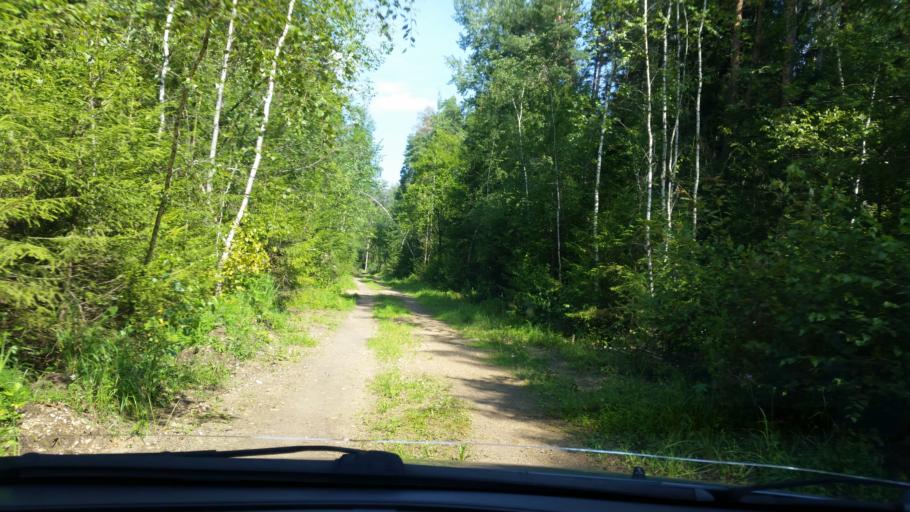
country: RU
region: Moskovskaya
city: Bol'shoye Gryzlovo
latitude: 54.9022
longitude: 37.7642
